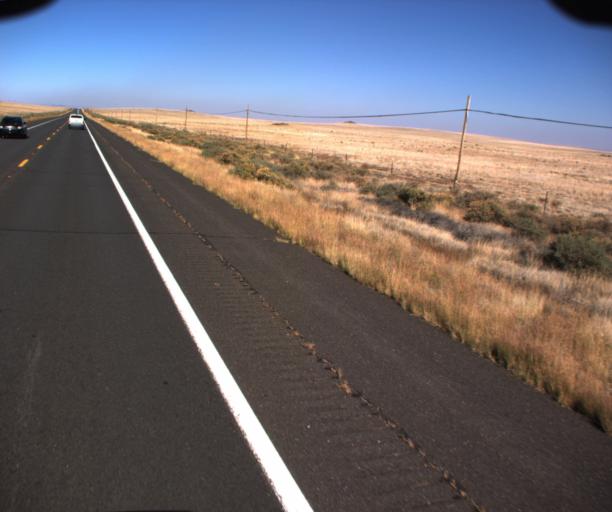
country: US
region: Arizona
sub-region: Coconino County
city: Flagstaff
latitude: 35.5969
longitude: -111.5265
